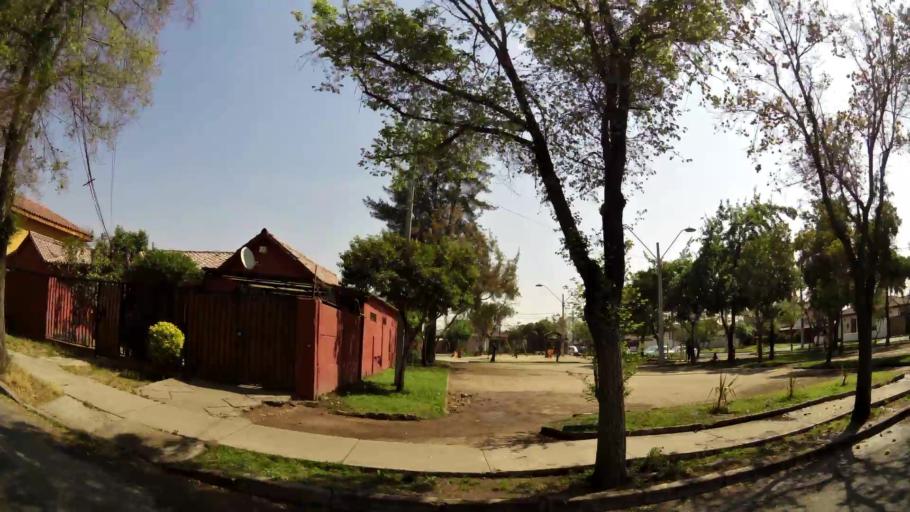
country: CL
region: Santiago Metropolitan
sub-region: Provincia de Santiago
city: La Pintana
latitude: -33.5495
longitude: -70.6017
